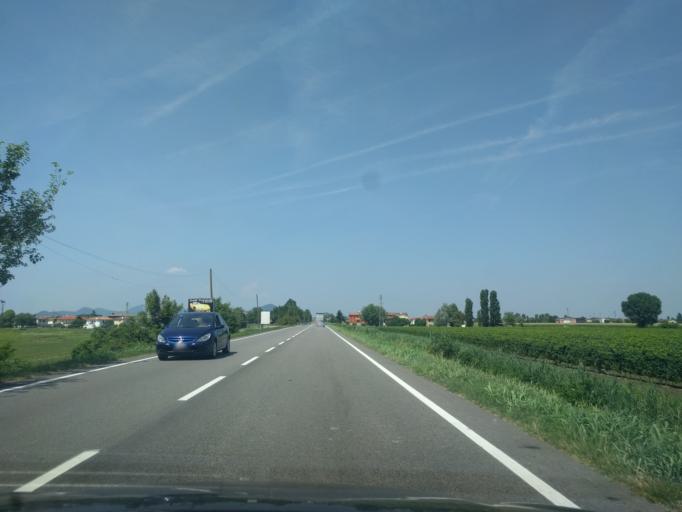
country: IT
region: Veneto
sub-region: Provincia di Padova
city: Solesino
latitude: 45.1662
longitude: 11.7563
